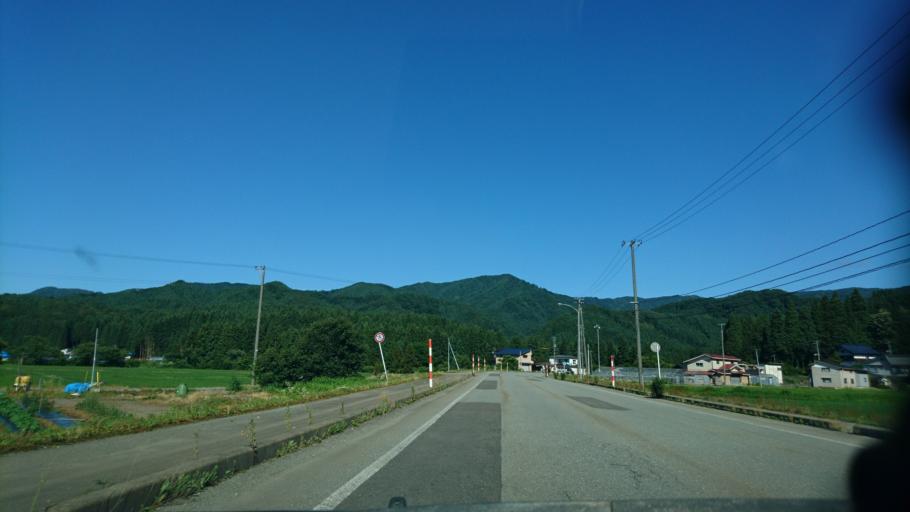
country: JP
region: Akita
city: Kakunodatemachi
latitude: 39.6819
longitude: 140.5592
